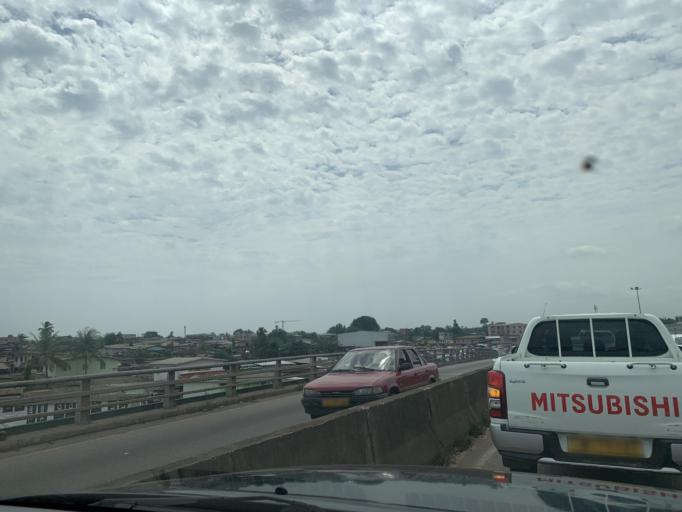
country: GA
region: Estuaire
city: Libreville
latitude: 0.3709
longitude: 9.4765
